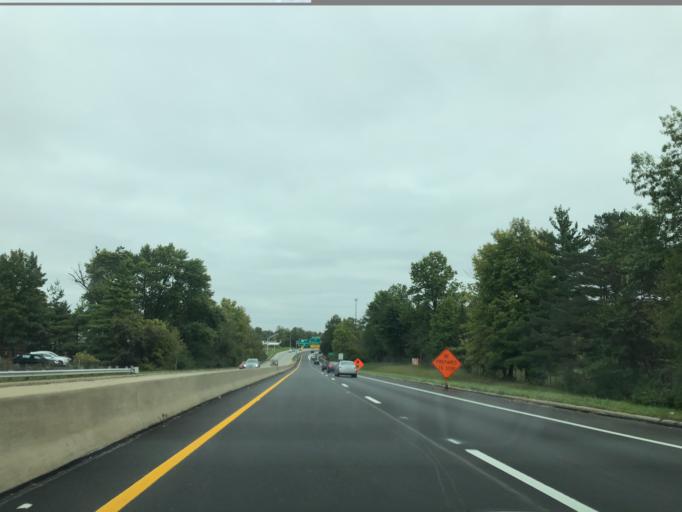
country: US
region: Ohio
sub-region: Hamilton County
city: Blue Ash
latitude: 39.2257
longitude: -84.3756
